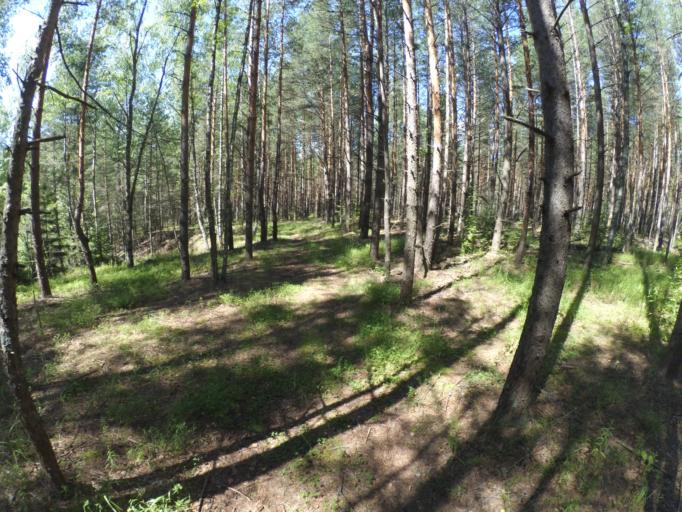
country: RU
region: Moskovskaya
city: Fosforitnyy
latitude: 55.3425
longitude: 38.9216
